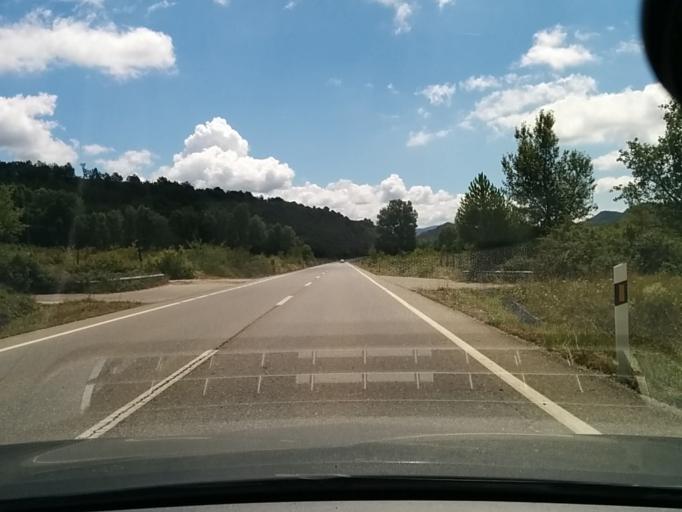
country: ES
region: Aragon
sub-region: Provincia de Huesca
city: Ainsa
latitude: 42.4258
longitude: 0.1211
